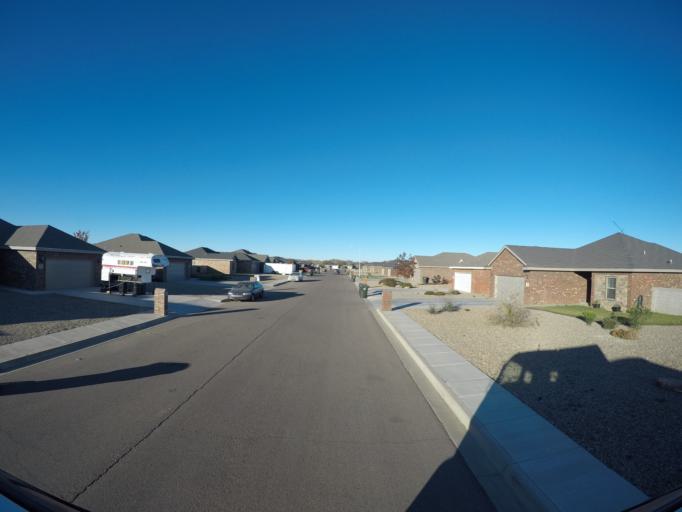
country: US
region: New Mexico
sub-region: Curry County
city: Clovis
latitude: 34.4090
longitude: -103.1705
